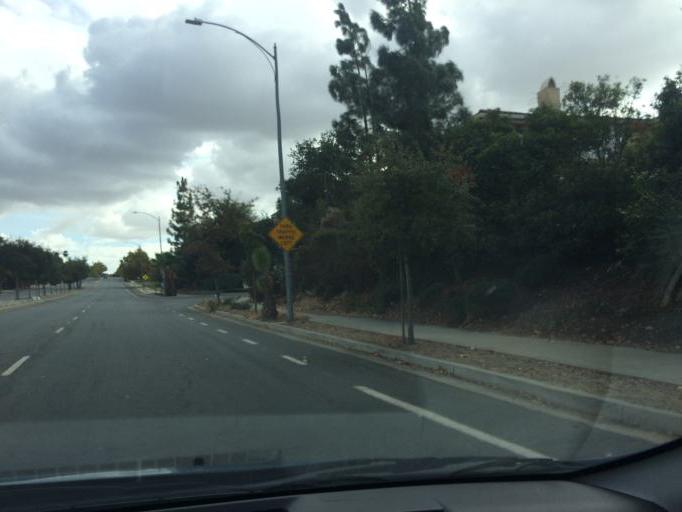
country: US
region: California
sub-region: Santa Clara County
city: Seven Trees
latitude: 37.2962
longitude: -121.7691
